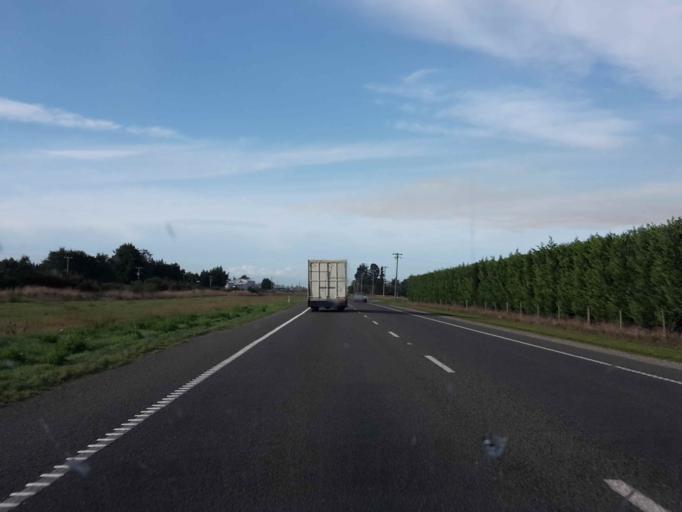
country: NZ
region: Canterbury
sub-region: Ashburton District
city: Tinwald
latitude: -43.9305
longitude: 171.7009
